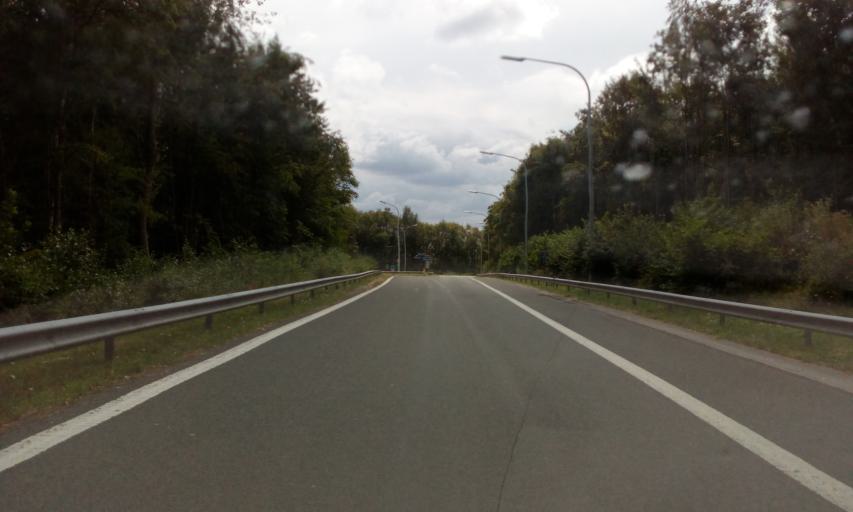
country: BE
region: Wallonia
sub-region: Province de Namur
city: Assesse
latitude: 50.3306
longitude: 5.0162
